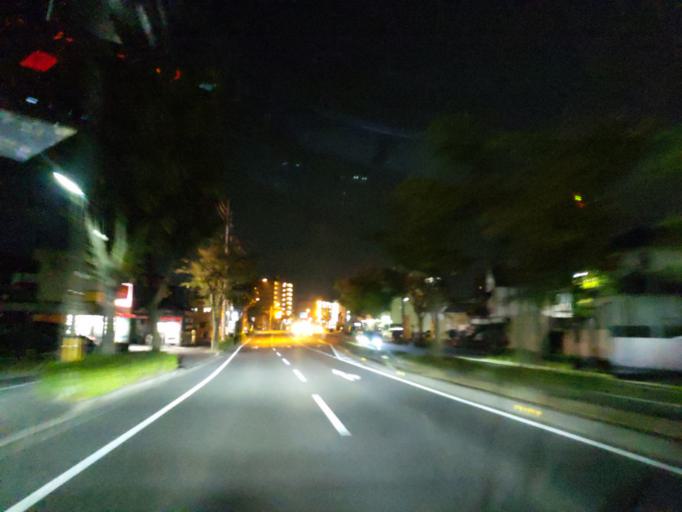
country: JP
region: Okayama
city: Okayama-shi
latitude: 34.6657
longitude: 133.9436
